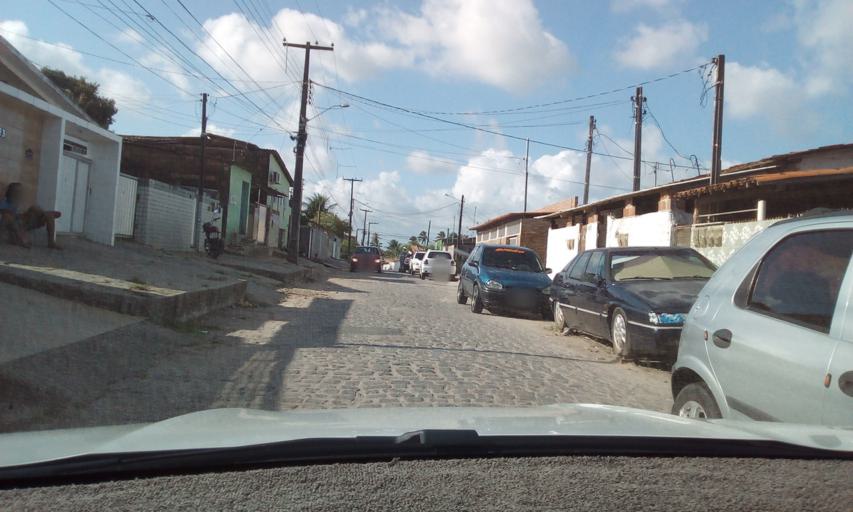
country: BR
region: Paraiba
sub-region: Joao Pessoa
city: Joao Pessoa
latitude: -7.1028
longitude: -34.8610
